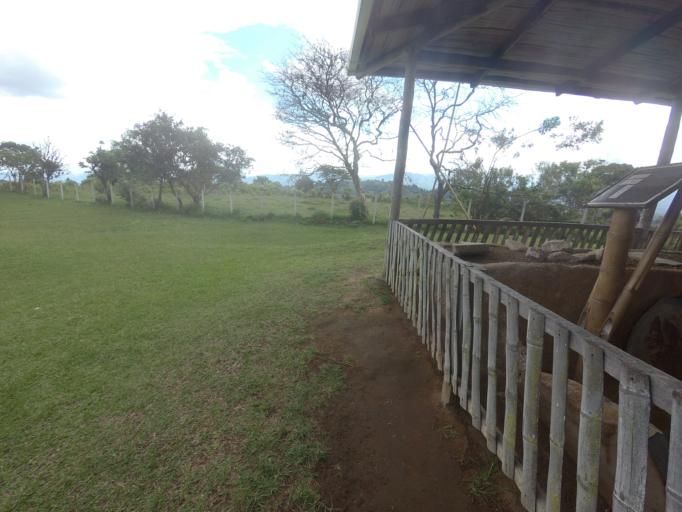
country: CO
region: Huila
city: Isnos
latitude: 1.9145
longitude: -76.2414
